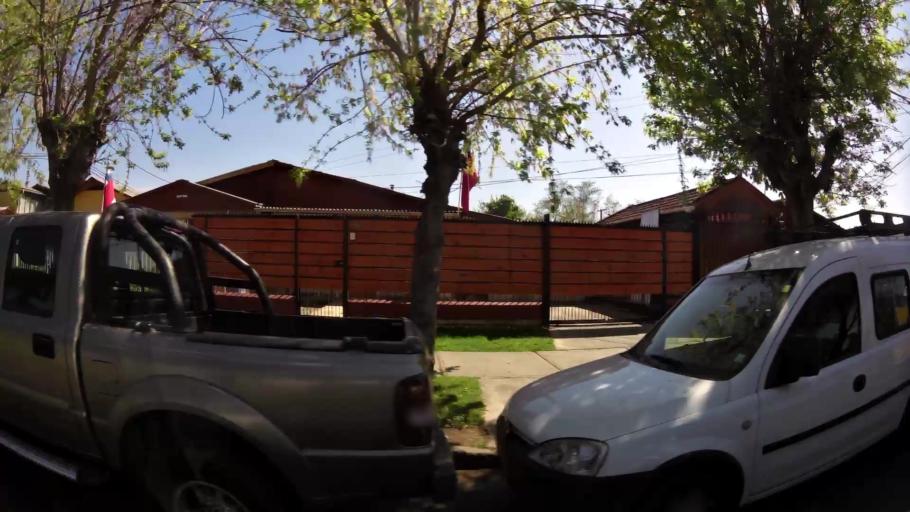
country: CL
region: Santiago Metropolitan
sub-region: Provincia de Santiago
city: Lo Prado
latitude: -33.5077
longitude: -70.7391
